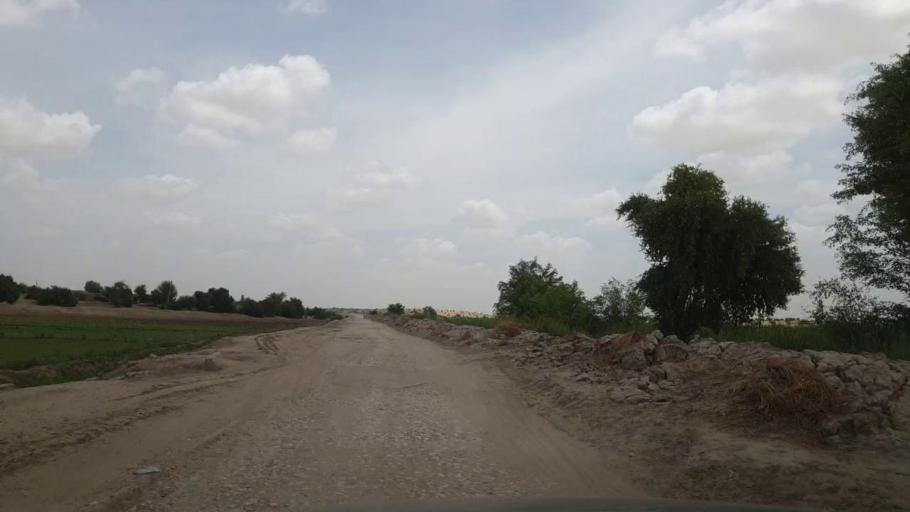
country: PK
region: Sindh
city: Kot Diji
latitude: 27.2030
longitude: 69.1210
